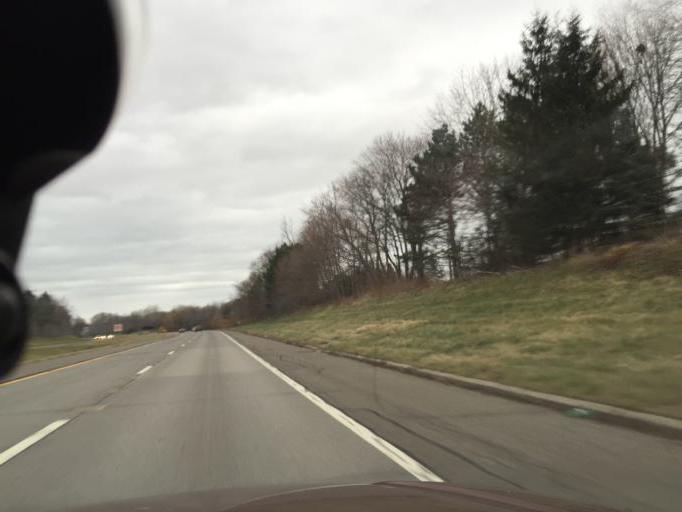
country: US
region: New York
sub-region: Monroe County
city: Greece
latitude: 43.2403
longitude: -77.6698
